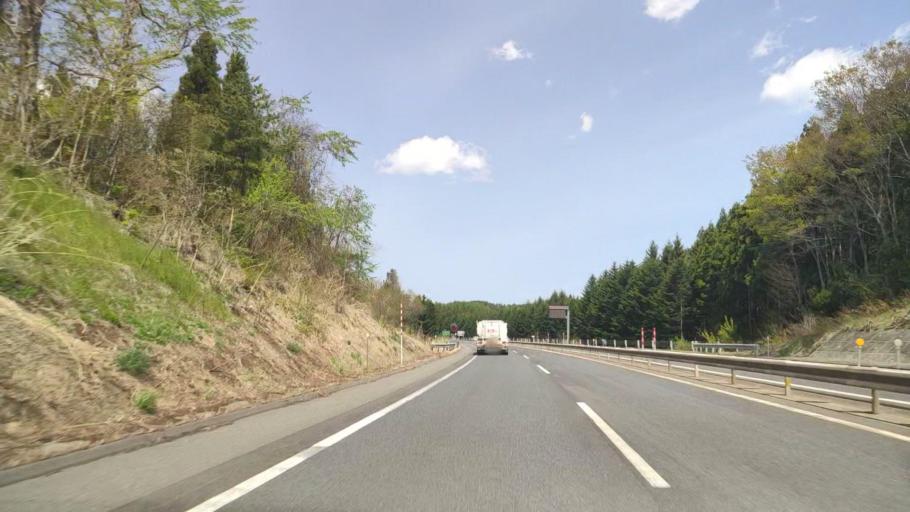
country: JP
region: Aomori
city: Hachinohe
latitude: 40.4109
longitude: 141.4438
